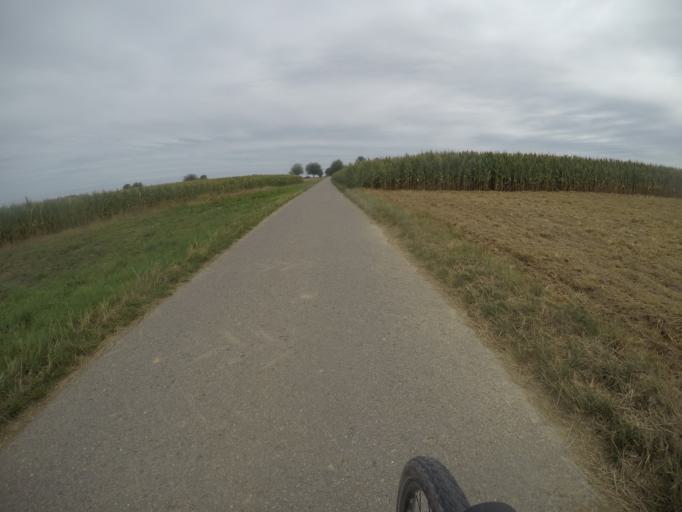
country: DE
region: Baden-Wuerttemberg
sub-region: Regierungsbezirk Stuttgart
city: Sersheim
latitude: 48.9469
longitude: 8.9997
